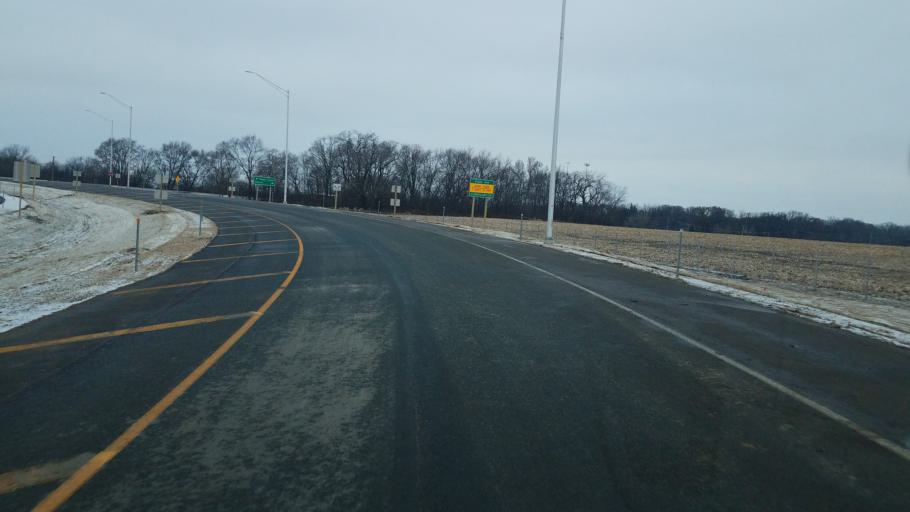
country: US
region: Illinois
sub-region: Kane County
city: Sugar Grove
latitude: 41.8198
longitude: -88.4645
